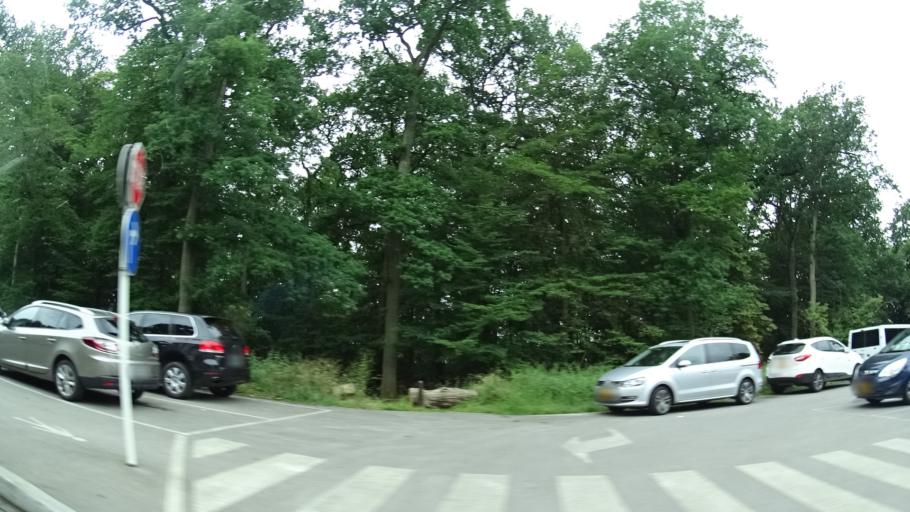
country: LU
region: Luxembourg
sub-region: Canton d'Esch-sur-Alzette
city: Bettembourg
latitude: 49.5093
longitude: 6.1189
